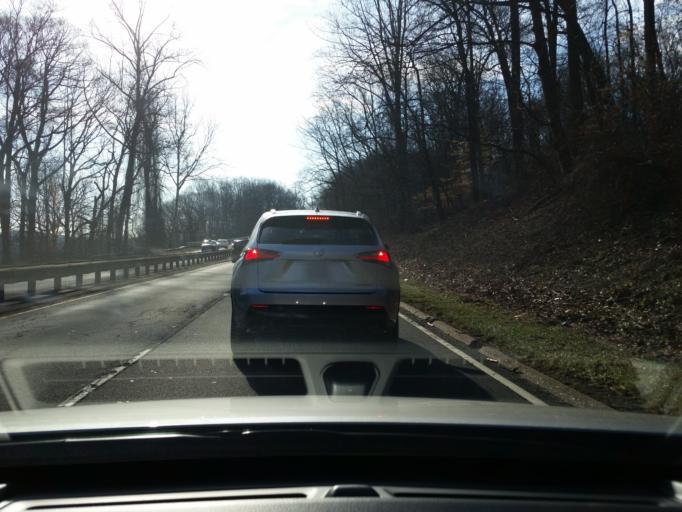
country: US
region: Maryland
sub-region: Montgomery County
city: Brookmont
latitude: 38.9297
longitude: -77.1201
